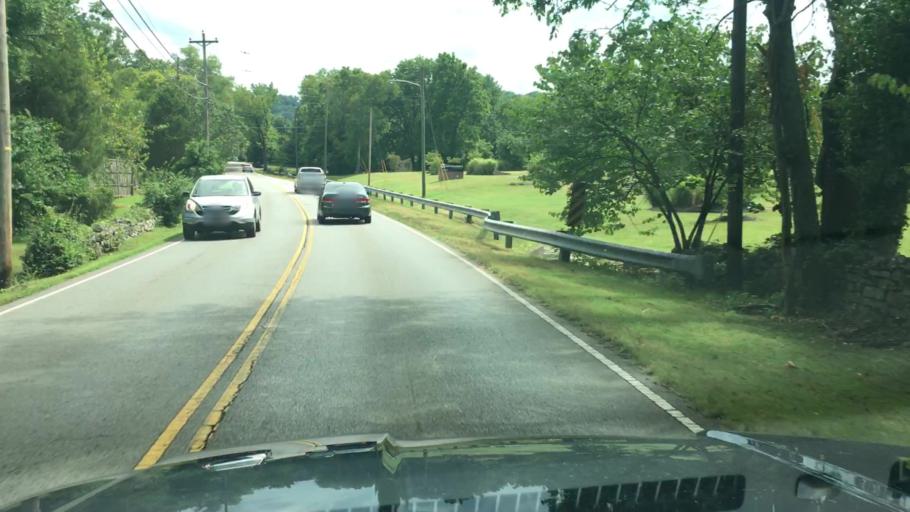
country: US
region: Tennessee
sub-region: Davidson County
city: Oak Hill
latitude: 36.0846
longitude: -86.8047
